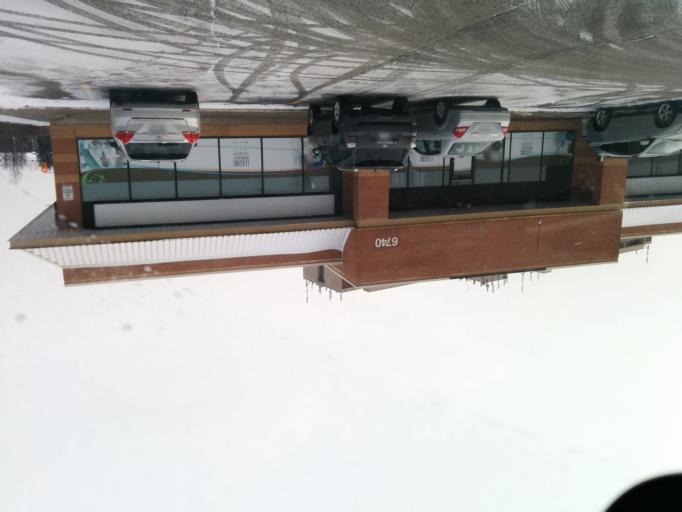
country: CA
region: Ontario
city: Brampton
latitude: 43.5836
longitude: -79.7614
